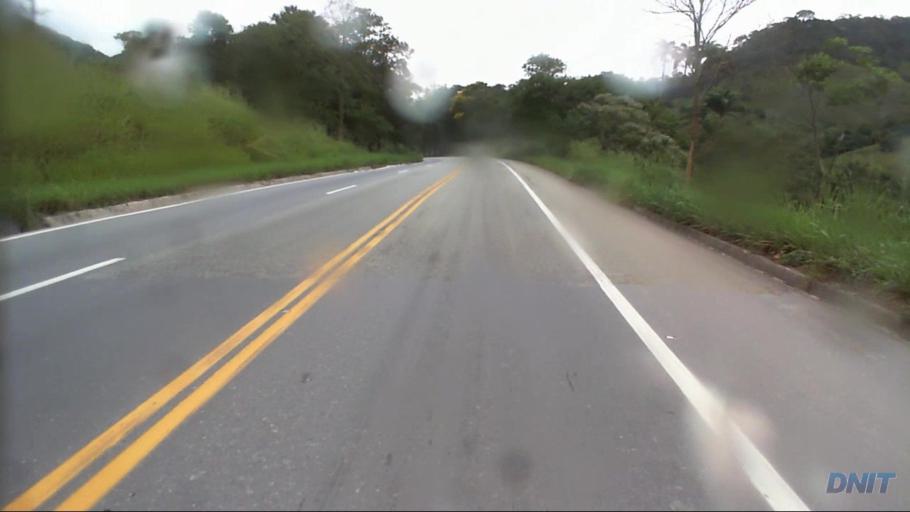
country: BR
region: Minas Gerais
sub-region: Nova Era
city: Nova Era
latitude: -19.7082
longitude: -42.9999
